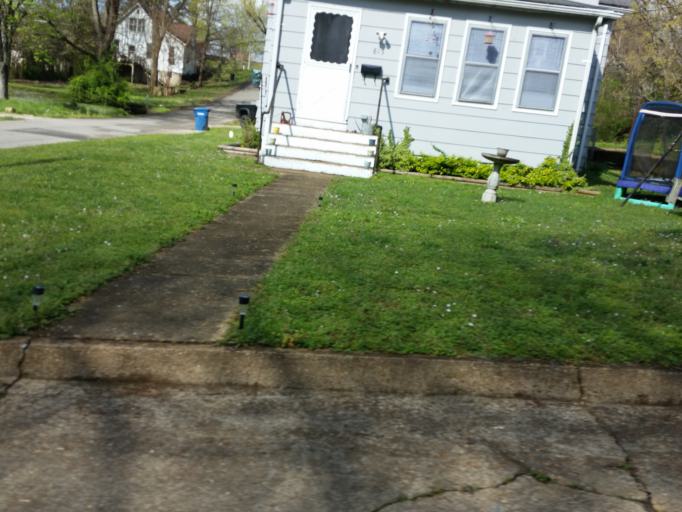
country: US
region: Missouri
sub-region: Butler County
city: Poplar Bluff
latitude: 36.7639
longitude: -90.3936
